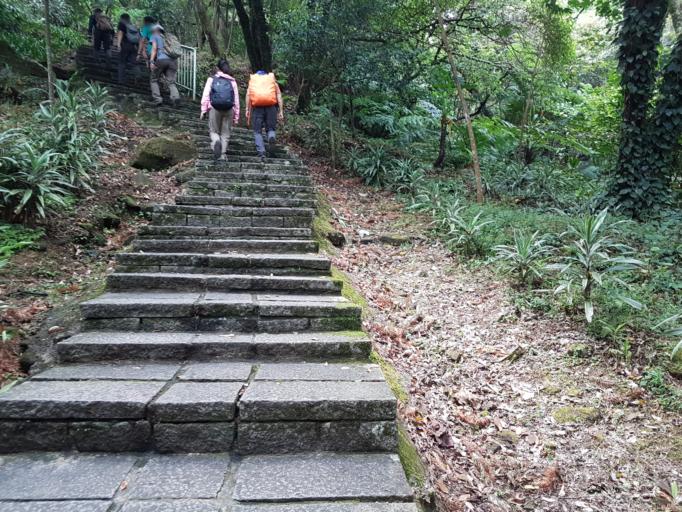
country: TW
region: Taiwan
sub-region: Keelung
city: Keelung
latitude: 25.0568
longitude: 121.6628
